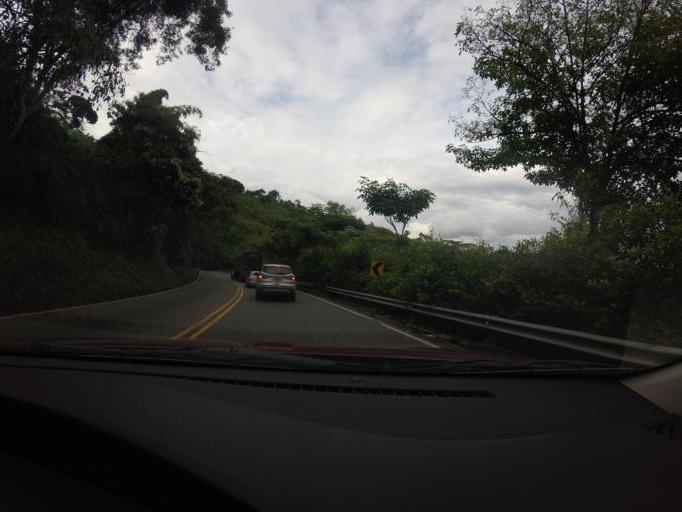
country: CO
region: Cundinamarca
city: Villeta
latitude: 5.0265
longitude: -74.5101
